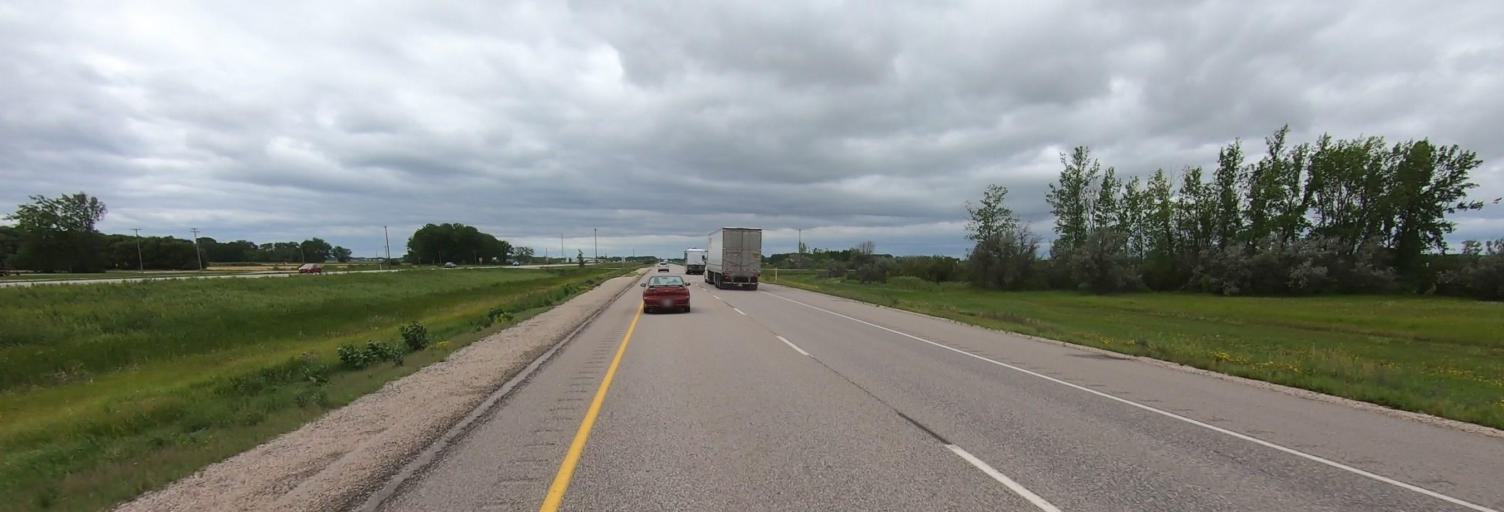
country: CA
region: Manitoba
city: Portage la Prairie
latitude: 49.9744
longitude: -98.1853
